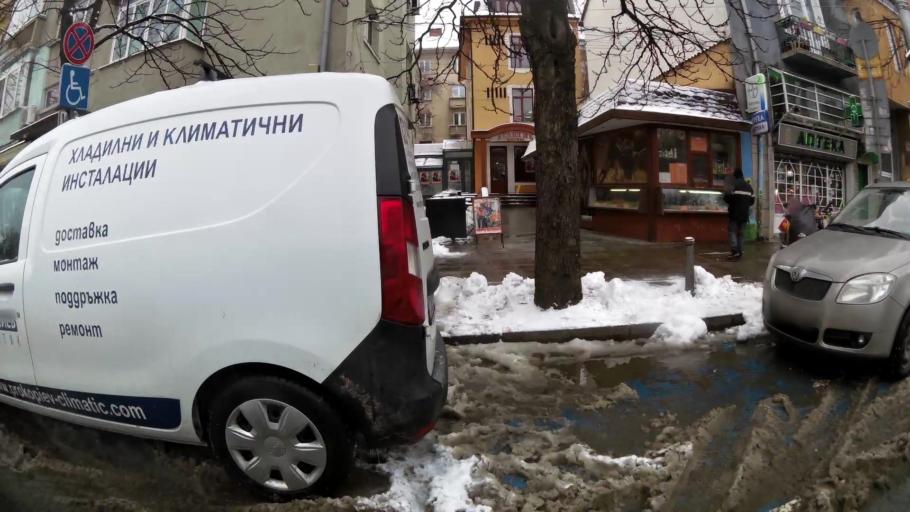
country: BG
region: Sofia-Capital
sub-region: Stolichna Obshtina
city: Sofia
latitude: 42.6960
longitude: 23.3453
